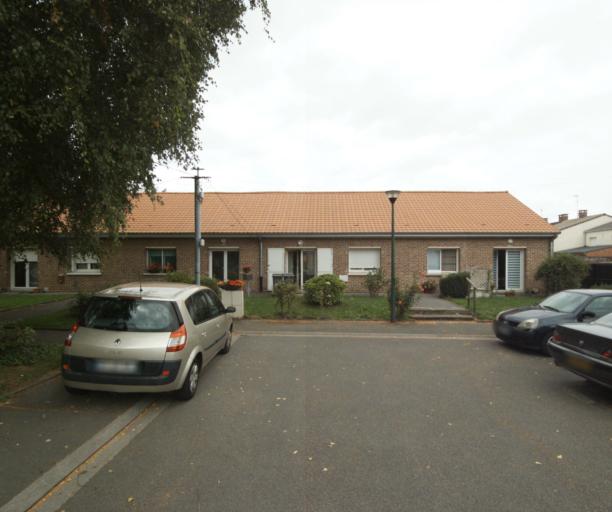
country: FR
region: Nord-Pas-de-Calais
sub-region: Departement du Nord
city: Forest-sur-Marque
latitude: 50.6334
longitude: 3.1915
